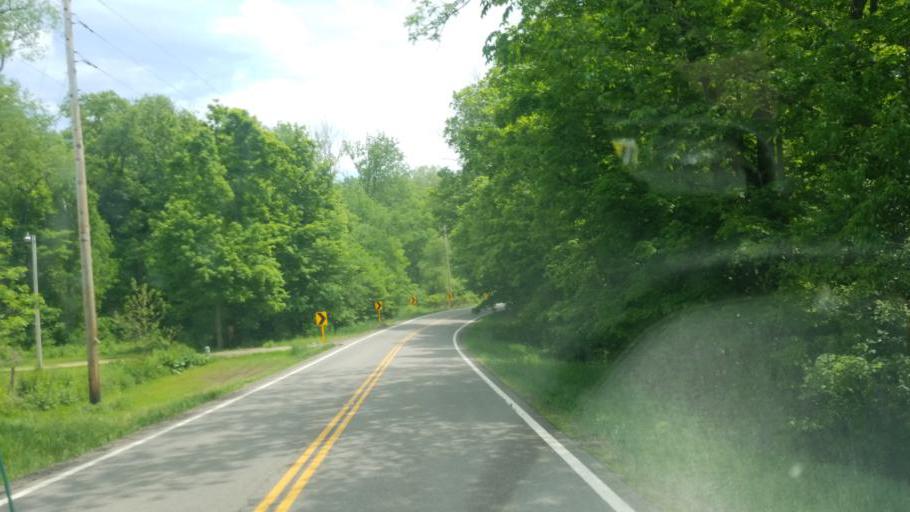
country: US
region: Ohio
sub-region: Ashland County
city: Ashland
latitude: 40.7492
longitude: -82.3533
